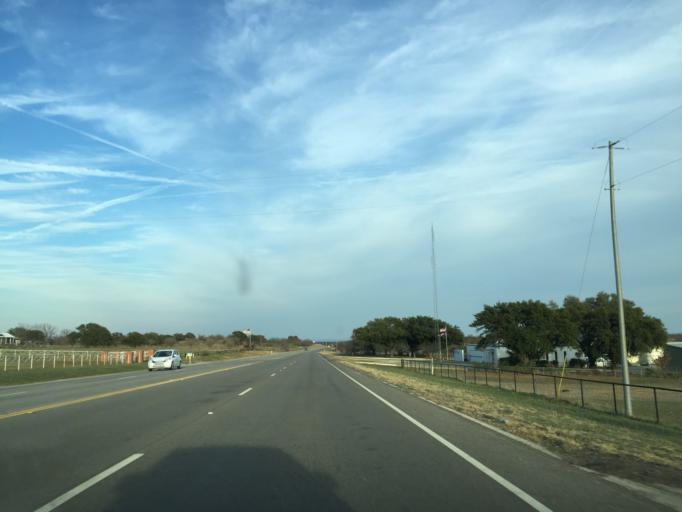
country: US
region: Texas
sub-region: Llano County
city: Llano
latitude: 30.7605
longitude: -98.6571
